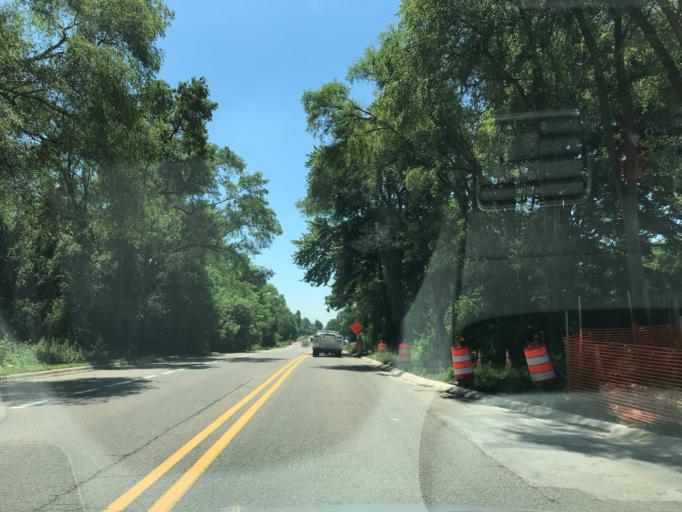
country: US
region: Michigan
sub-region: Oakland County
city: Franklin
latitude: 42.5086
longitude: -83.3396
